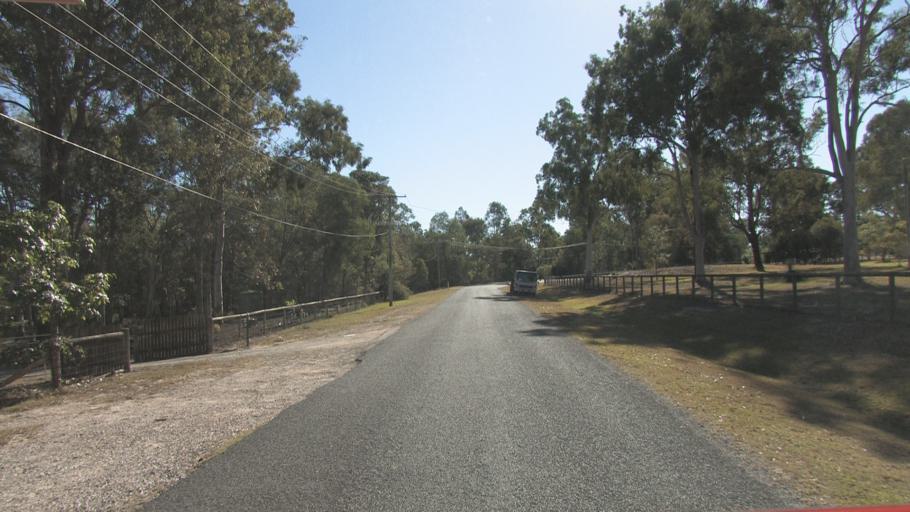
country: AU
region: Queensland
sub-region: Logan
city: Chambers Flat
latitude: -27.7911
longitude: 153.1289
